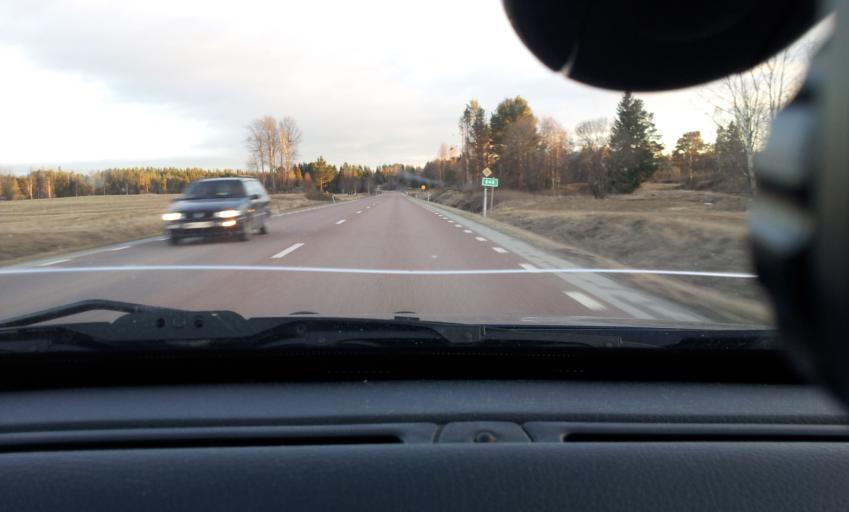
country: SE
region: Jaemtland
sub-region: Bergs Kommun
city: Hoverberg
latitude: 62.9692
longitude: 14.5589
